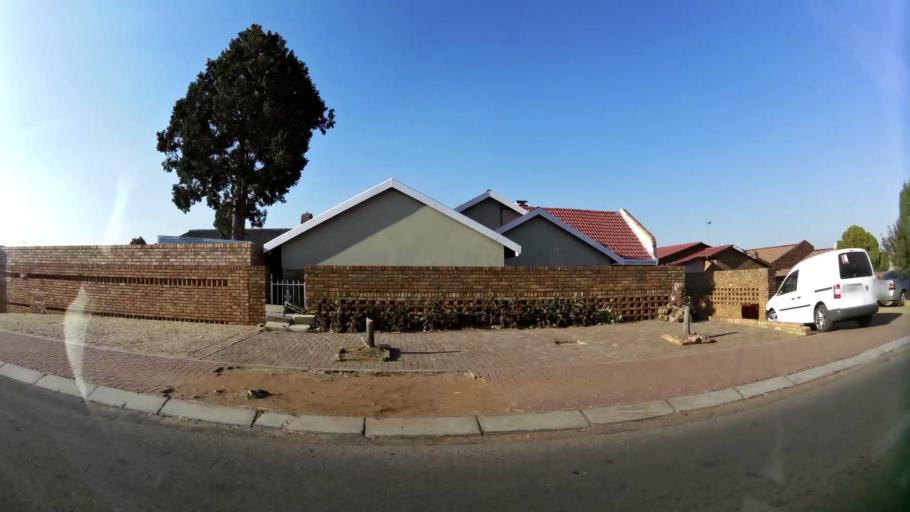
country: ZA
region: Gauteng
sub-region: City of Johannesburg Metropolitan Municipality
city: Soweto
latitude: -26.2668
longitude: 27.8730
